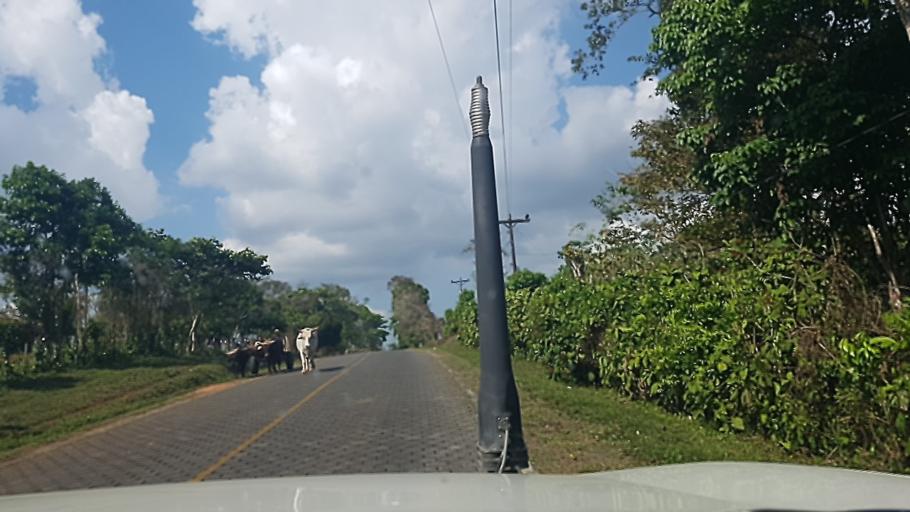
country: NI
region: Atlantico Sur
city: Nueva Guinea
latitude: 11.7061
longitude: -84.3679
